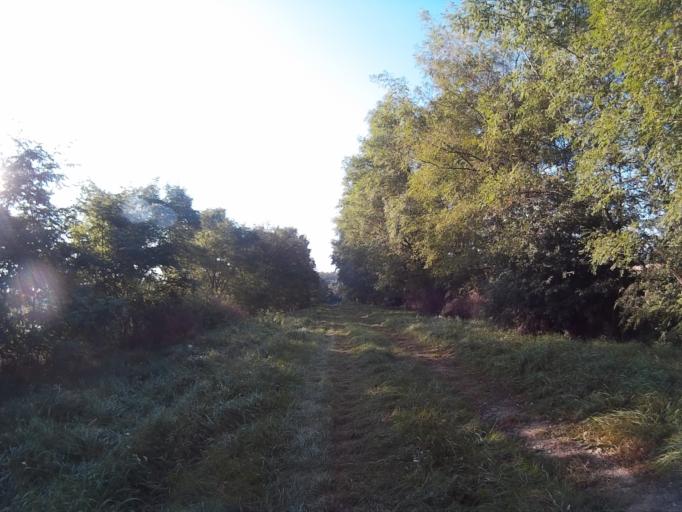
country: HU
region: Vas
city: Jak
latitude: 47.1170
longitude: 16.5922
